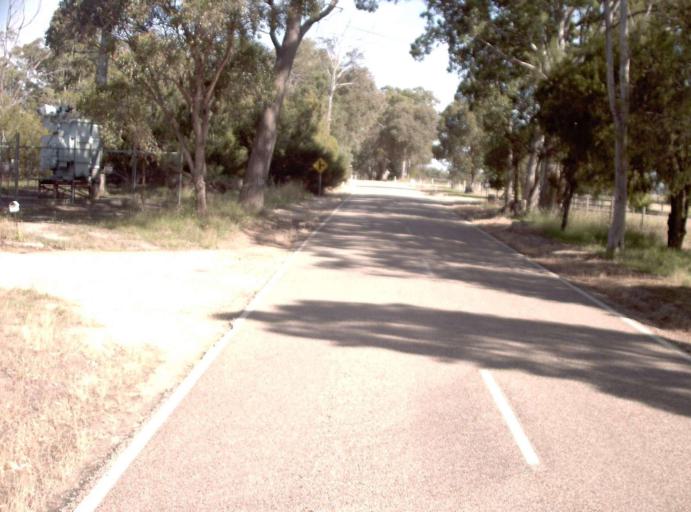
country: AU
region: Victoria
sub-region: East Gippsland
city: Lakes Entrance
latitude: -37.7832
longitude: 147.8265
